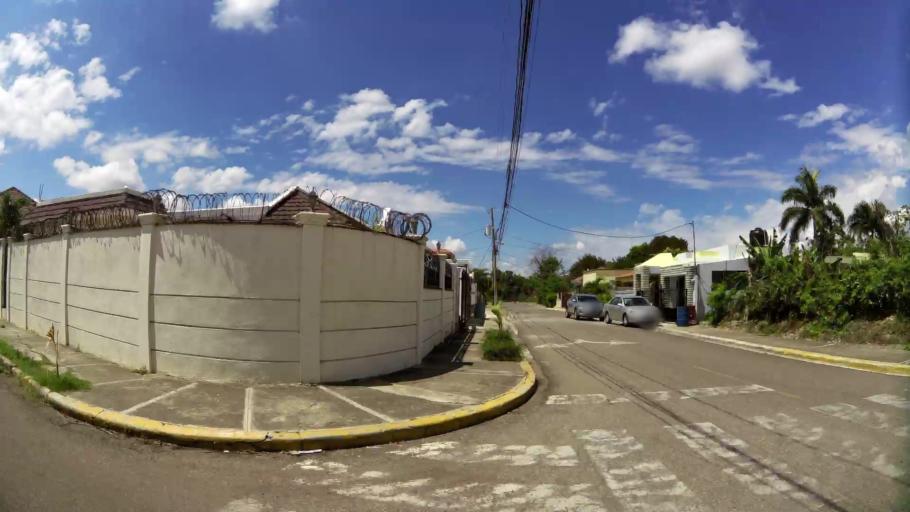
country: DO
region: Santiago
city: Santiago de los Caballeros
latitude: 19.4631
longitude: -70.6642
